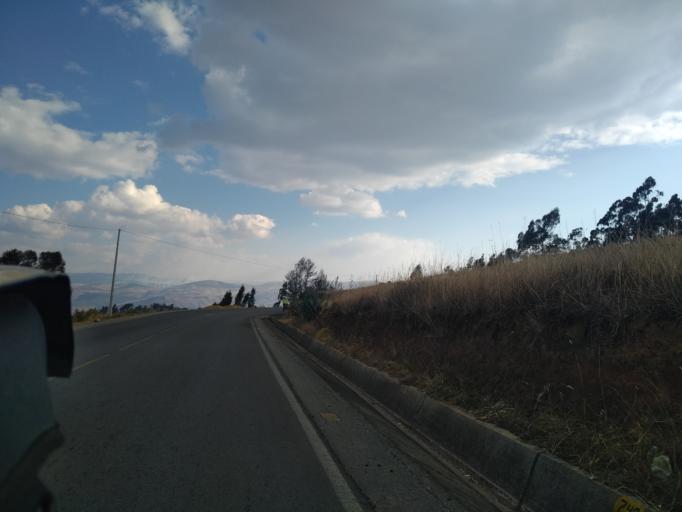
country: PE
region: Cajamarca
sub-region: Provincia de Cajamarca
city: Llacanora
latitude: -7.1510
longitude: -78.4126
